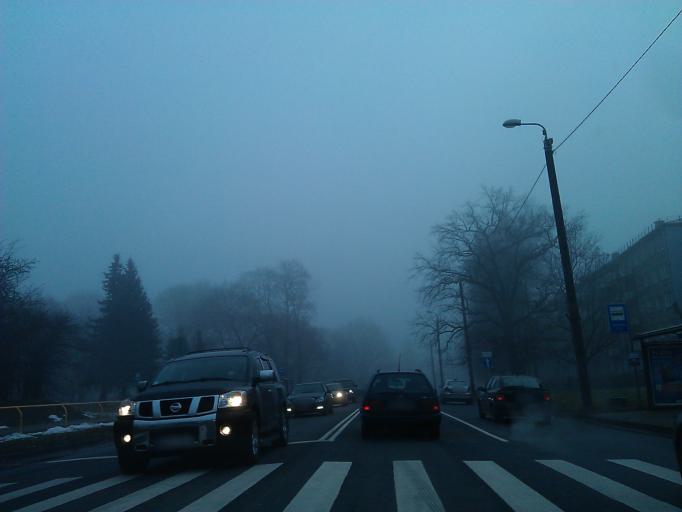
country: LV
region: Riga
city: Bergi
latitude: 56.9830
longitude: 24.2504
